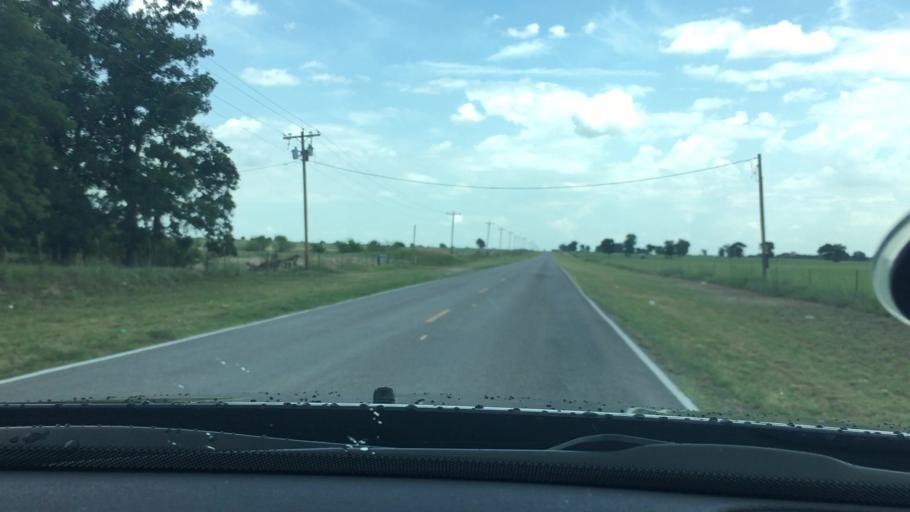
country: US
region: Oklahoma
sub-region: Carter County
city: Wilson
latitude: 33.9403
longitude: -97.4008
